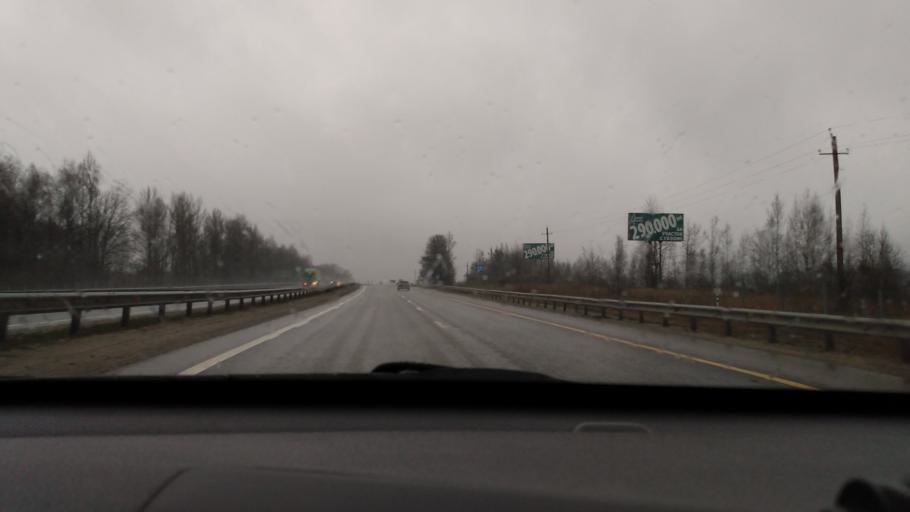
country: RU
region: Moskovskaya
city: Ozherel'ye
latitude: 54.5781
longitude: 38.1652
